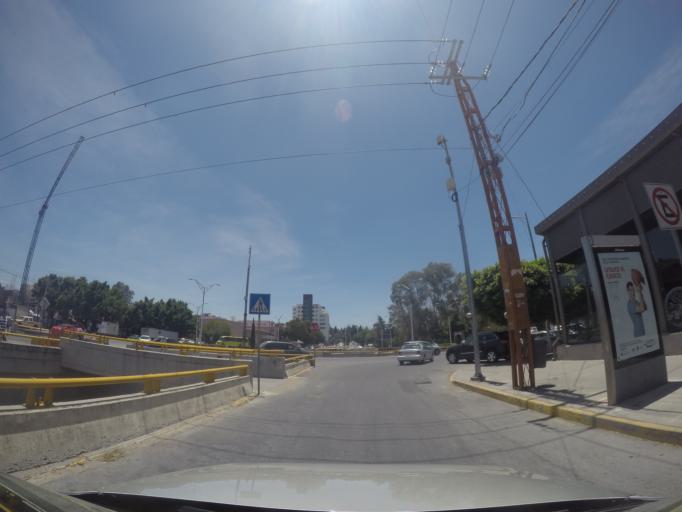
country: MX
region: San Luis Potosi
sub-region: San Luis Potosi
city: San Luis Potosi
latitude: 22.1486
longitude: -101.0143
